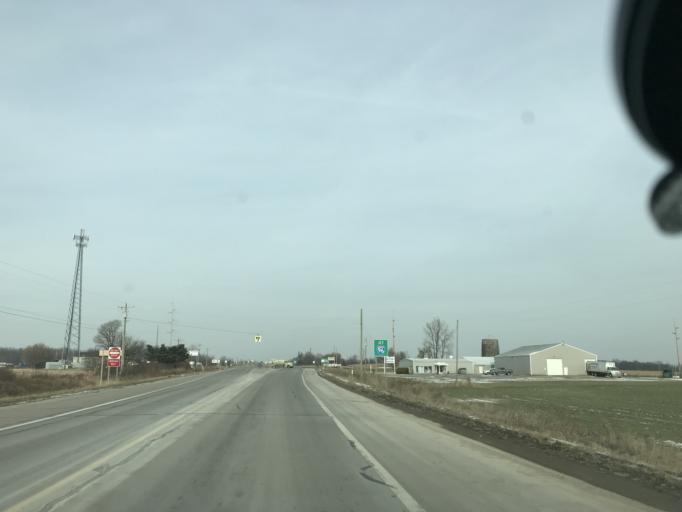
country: US
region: Michigan
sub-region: Ionia County
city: Lake Odessa
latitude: 42.8724
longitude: -85.0750
